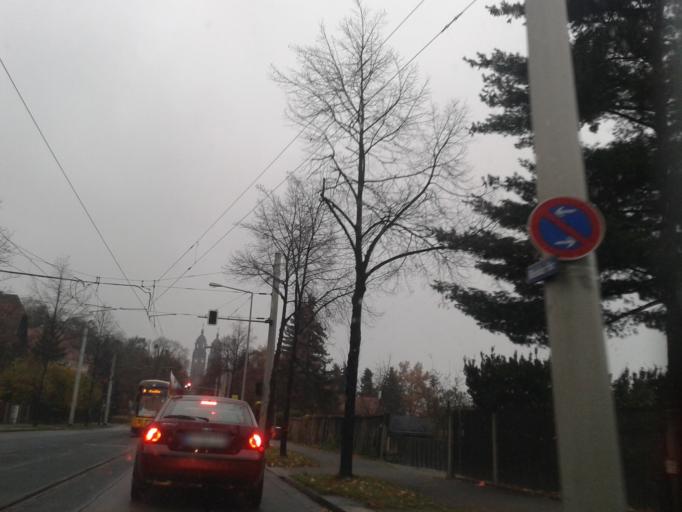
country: DE
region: Saxony
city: Dresden
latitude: 51.0244
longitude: 13.7712
